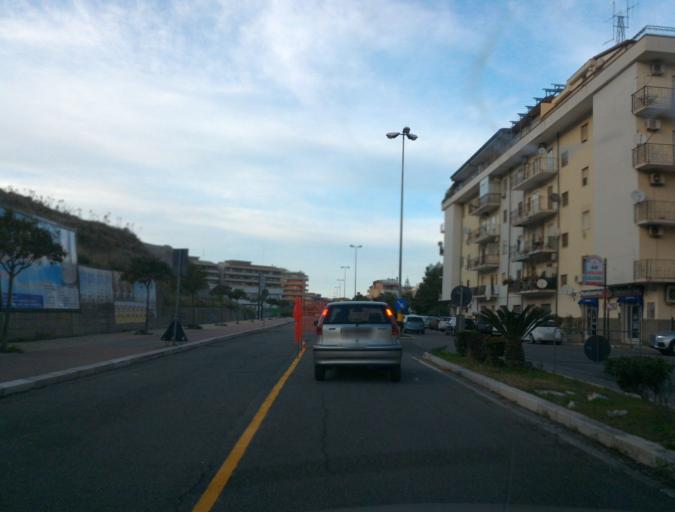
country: IT
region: Calabria
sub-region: Provincia di Crotone
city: Crotone
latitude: 39.0684
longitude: 17.1288
